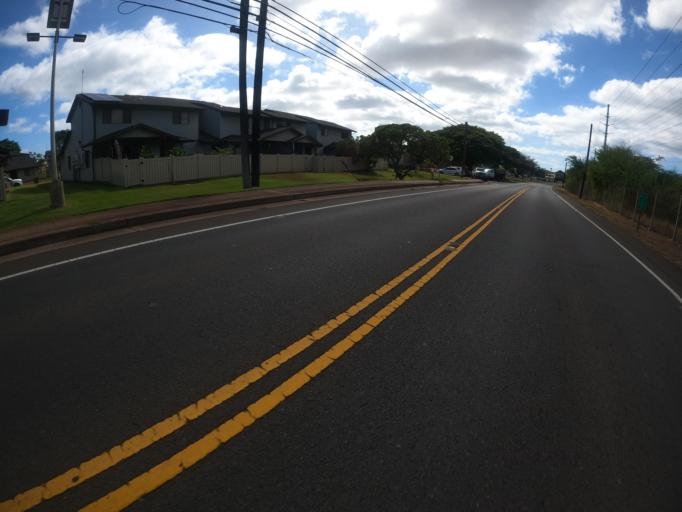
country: US
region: Hawaii
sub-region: Honolulu County
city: Makakilo City
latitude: 21.3230
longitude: -158.0743
